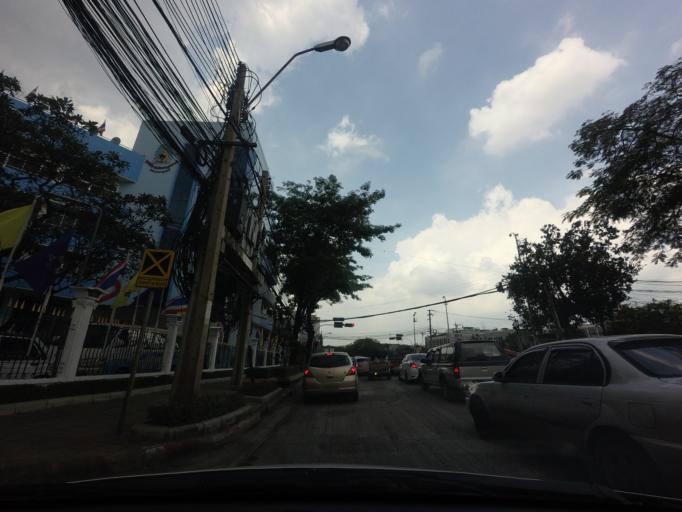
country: TH
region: Bangkok
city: Pom Prap Sattru Phai
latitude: 13.7562
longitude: 100.5163
